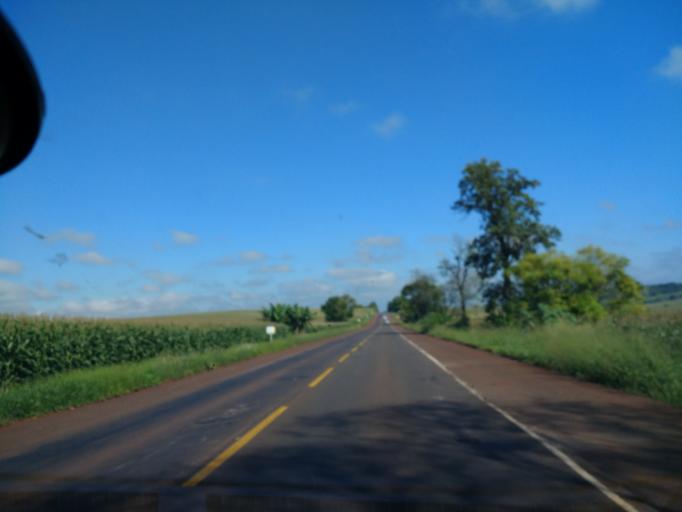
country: BR
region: Parana
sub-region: Paicandu
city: Paicandu
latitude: -23.5071
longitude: -52.1634
